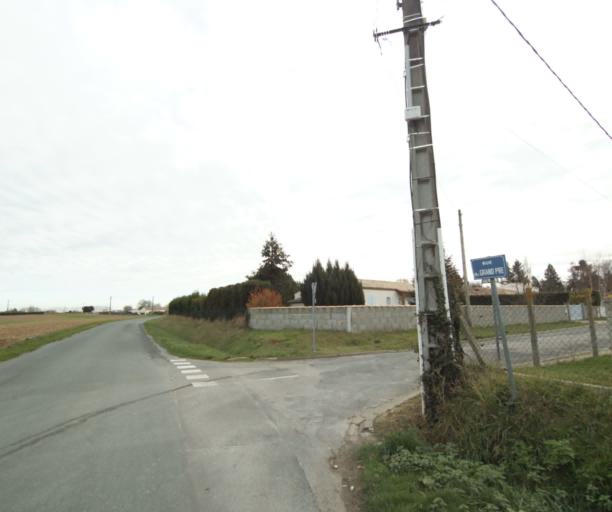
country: FR
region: Poitou-Charentes
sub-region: Departement de la Charente-Maritime
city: Corme-Royal
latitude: 45.7436
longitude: -0.8060
